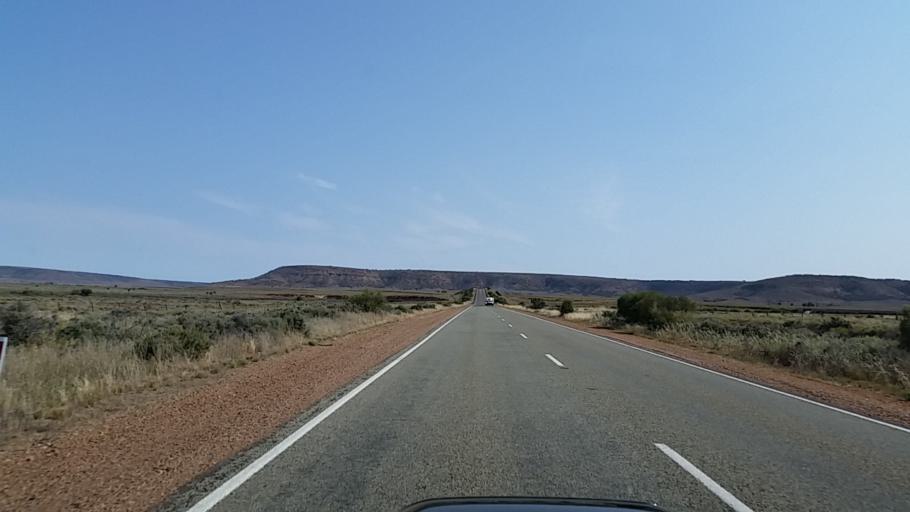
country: AU
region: South Australia
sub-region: Port Augusta
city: Port Augusta West
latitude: -32.5382
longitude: 137.6475
